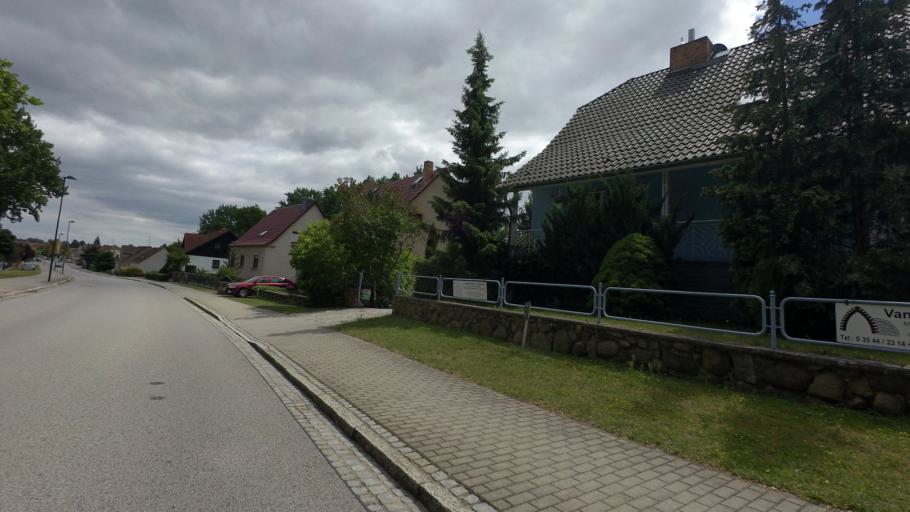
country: DE
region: Brandenburg
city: Luckau
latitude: 51.8511
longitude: 13.6990
